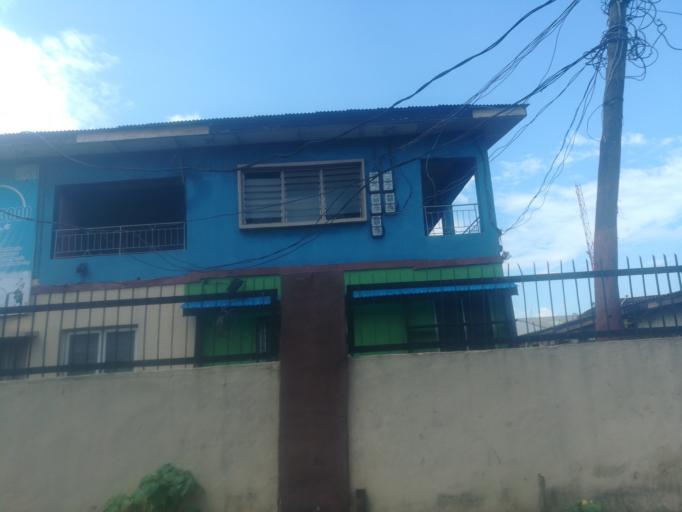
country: NG
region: Lagos
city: Ojota
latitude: 6.5637
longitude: 3.3676
